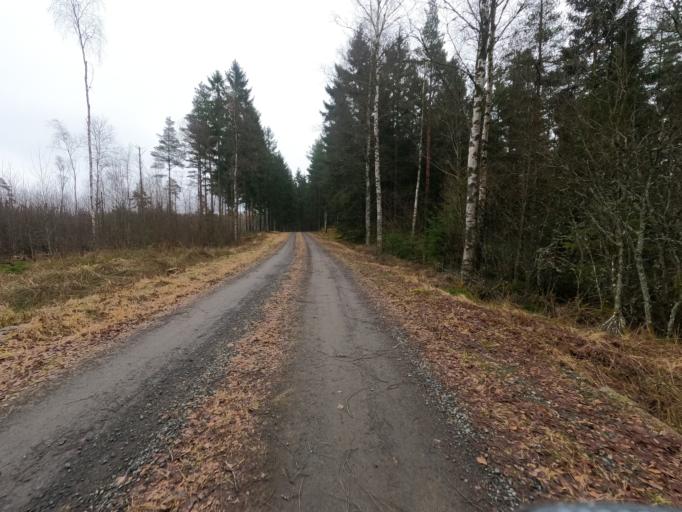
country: SE
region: Kronoberg
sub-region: Markaryds Kommun
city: Stromsnasbruk
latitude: 56.8095
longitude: 13.5674
